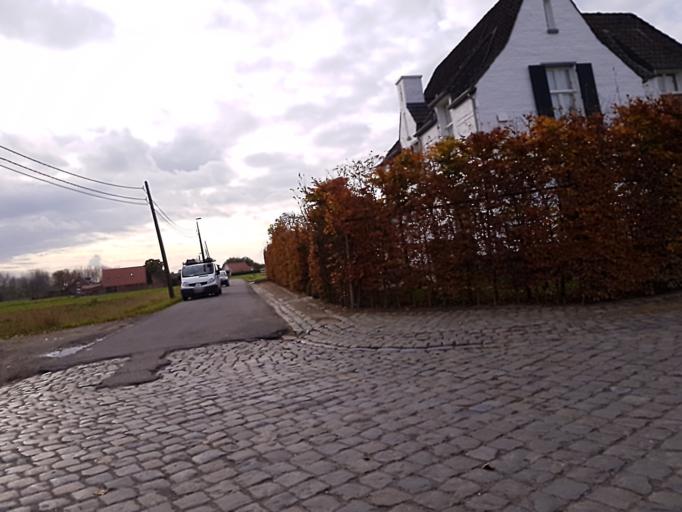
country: BE
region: Flanders
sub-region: Provincie Antwerpen
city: Duffel
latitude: 51.1172
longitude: 4.5251
